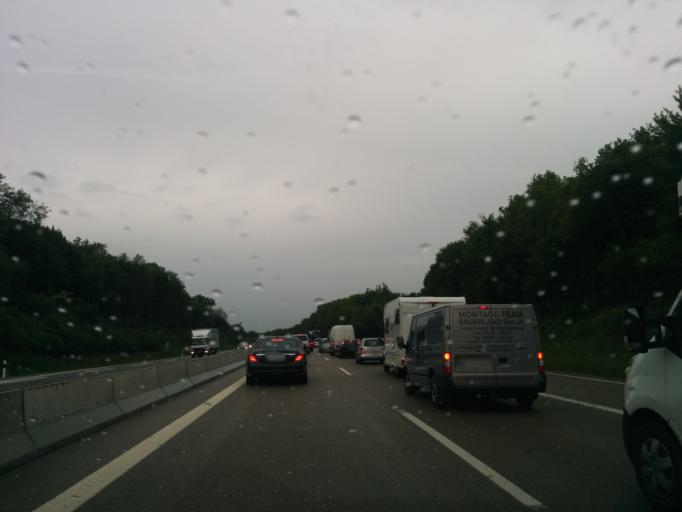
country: DE
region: Bavaria
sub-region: Regierungsbezirk Unterfranken
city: Martinsheim
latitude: 49.6224
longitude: 10.1747
